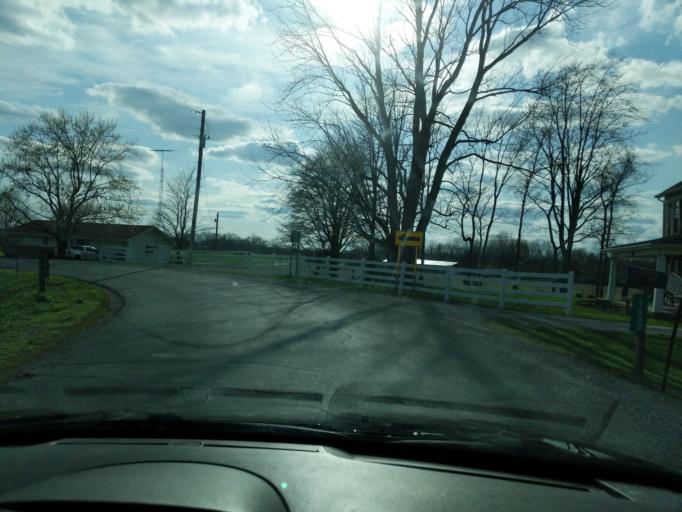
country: US
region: Ohio
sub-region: Champaign County
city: Urbana
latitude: 40.1323
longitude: -83.7285
